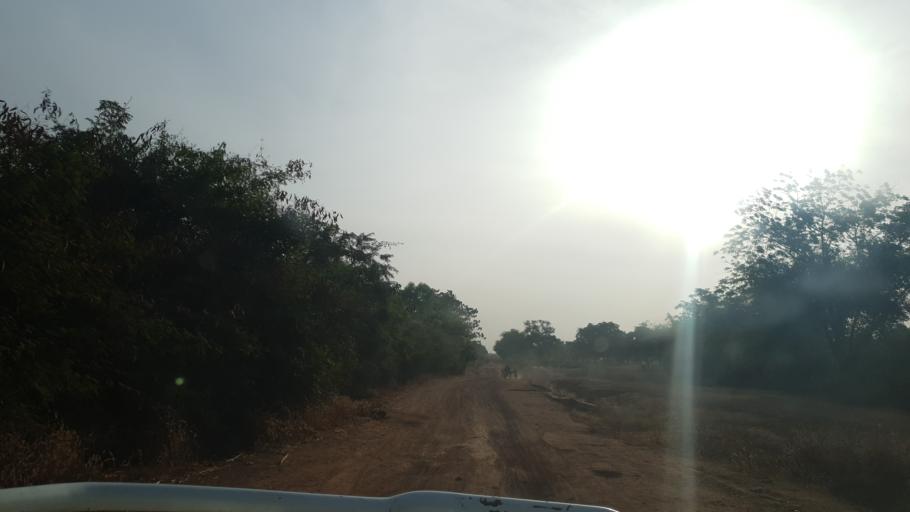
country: ML
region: Koulikoro
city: Dioila
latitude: 12.7708
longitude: -6.9331
